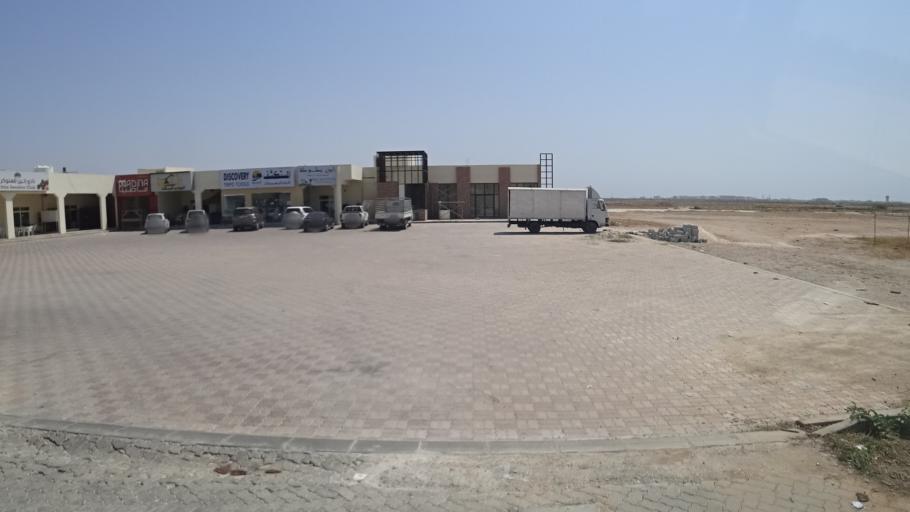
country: OM
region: Zufar
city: Salalah
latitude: 17.0434
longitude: 54.0628
